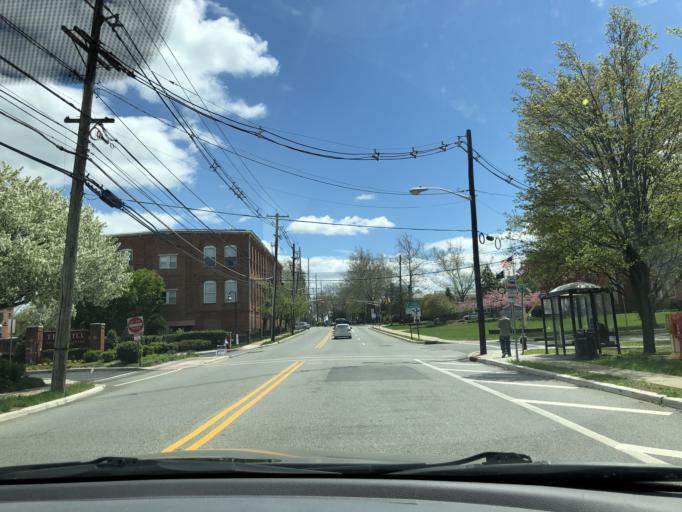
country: US
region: New Jersey
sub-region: Passaic County
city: Singac
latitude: 40.8833
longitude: -74.2349
